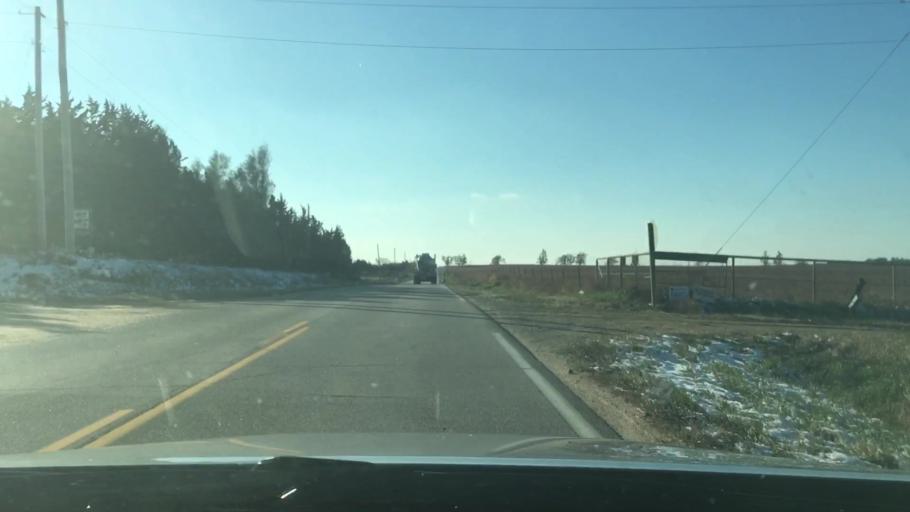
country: US
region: Kansas
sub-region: Reno County
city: Nickerson
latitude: 38.1449
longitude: -98.1422
